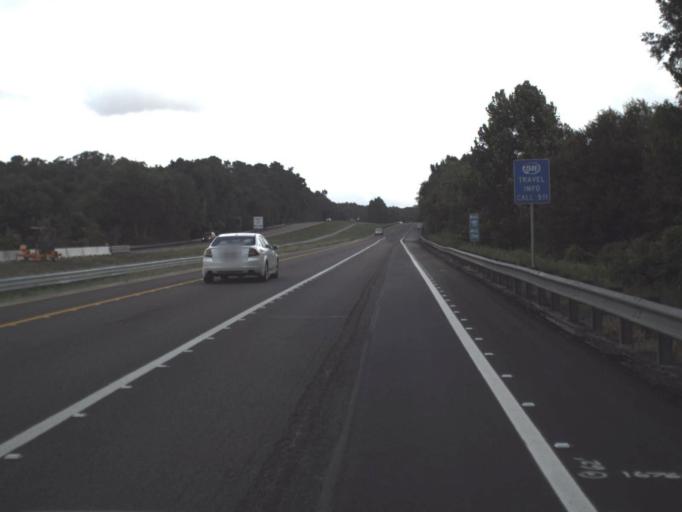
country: US
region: Florida
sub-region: Hernando County
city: Hill 'n Dale
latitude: 28.4351
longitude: -82.2809
